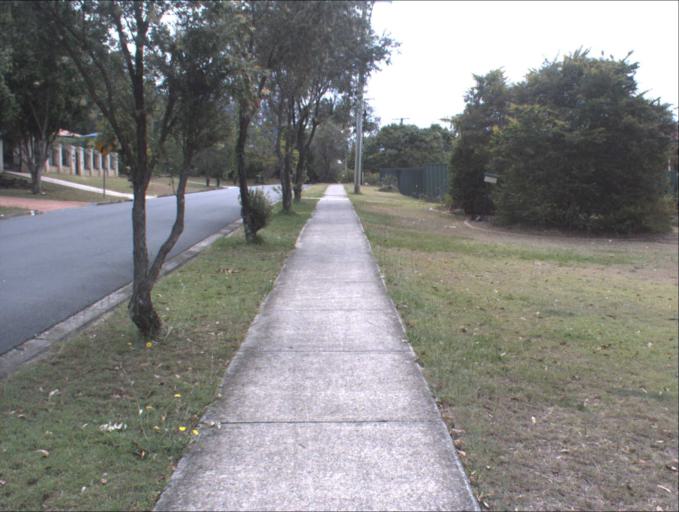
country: AU
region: Queensland
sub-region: Logan
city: Slacks Creek
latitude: -27.6725
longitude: 153.1756
